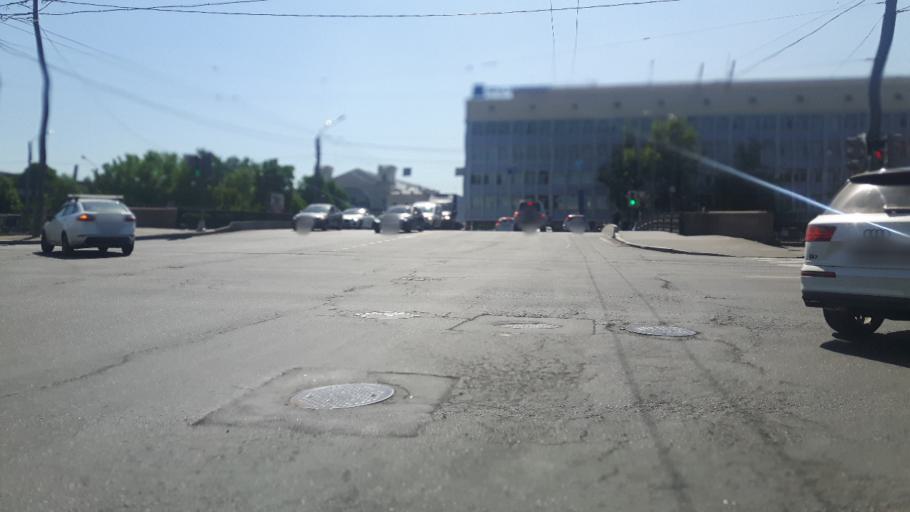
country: RU
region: St.-Petersburg
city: Admiralteisky
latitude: 59.9094
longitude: 30.2977
